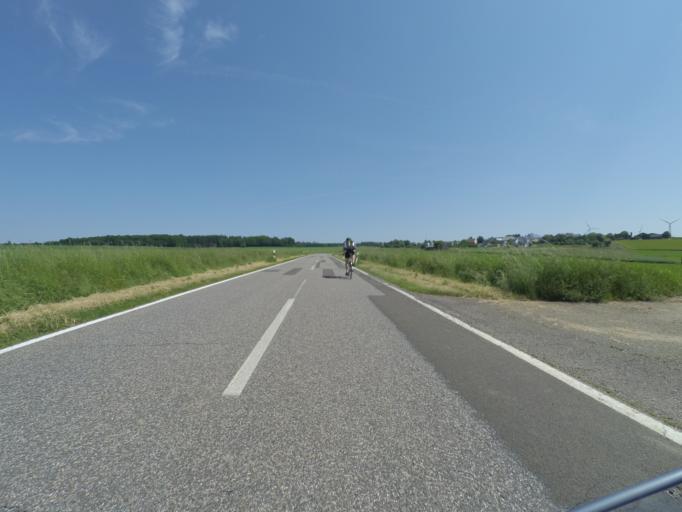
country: DE
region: Rheinland-Pfalz
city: Spesenroth
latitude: 50.0466
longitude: 7.4526
